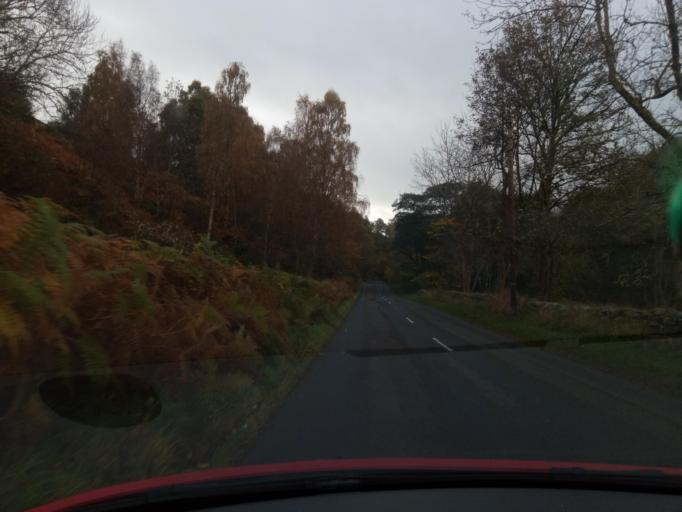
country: GB
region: Scotland
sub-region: The Scottish Borders
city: Galashiels
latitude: 55.6099
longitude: -2.8766
